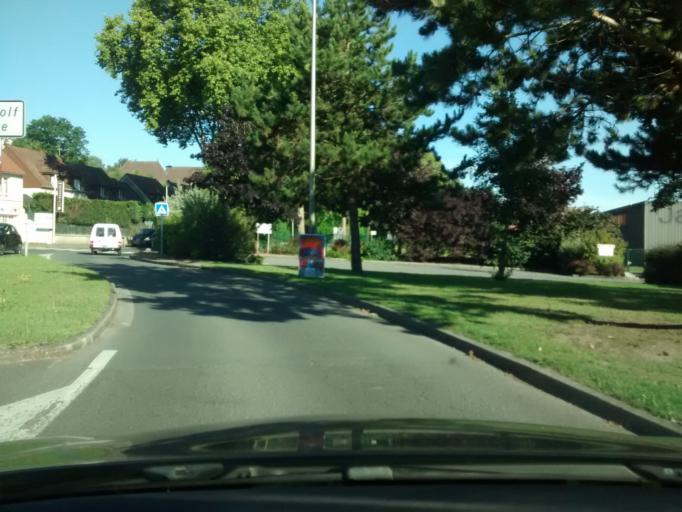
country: FR
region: Lower Normandy
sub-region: Departement du Calvados
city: Touques
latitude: 49.3455
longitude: 0.0842
